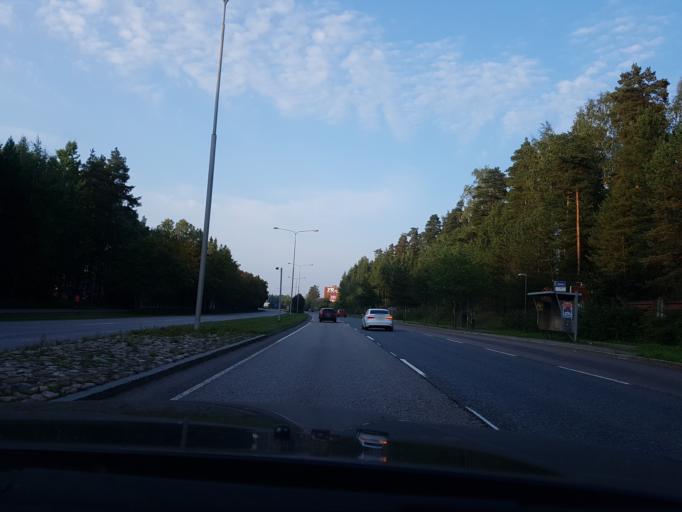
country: FI
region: Uusimaa
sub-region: Helsinki
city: Tuusula
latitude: 60.3796
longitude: 25.0237
